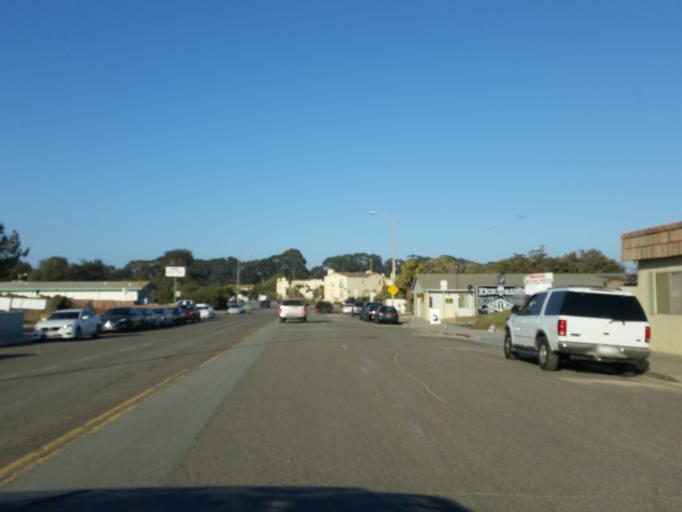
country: US
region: California
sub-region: San Luis Obispo County
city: Grover Beach
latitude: 35.1058
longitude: -120.6292
